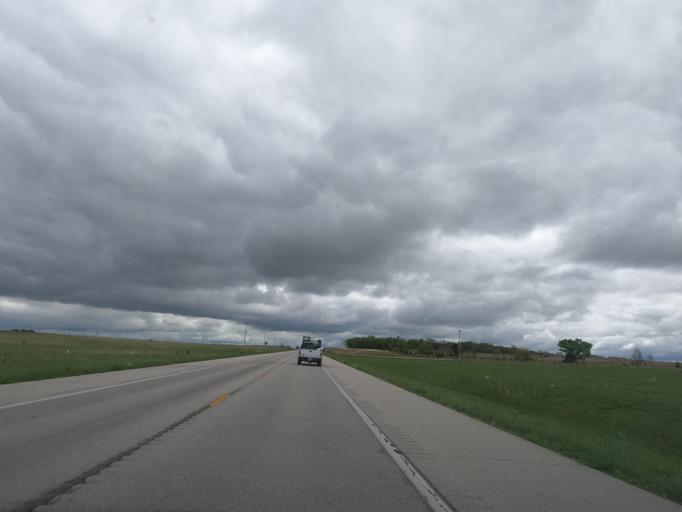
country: US
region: Kansas
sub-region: Wilson County
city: Fredonia
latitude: 37.5023
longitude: -95.7756
